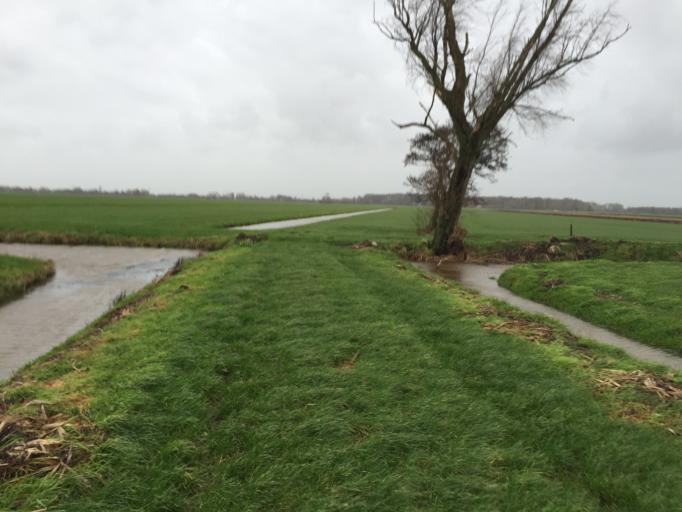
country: NL
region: Utrecht
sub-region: Gemeente Montfoort
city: Montfoort
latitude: 52.0422
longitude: 4.9150
